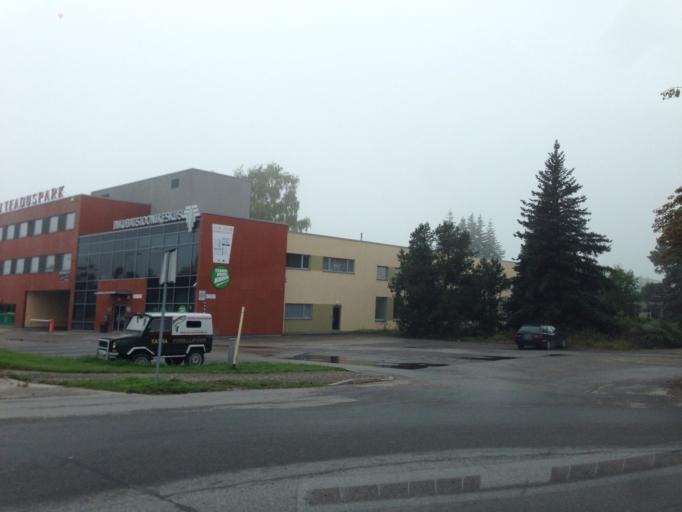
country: EE
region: Tartu
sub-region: Tartu linn
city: Tartu
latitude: 58.3563
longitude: 26.6806
